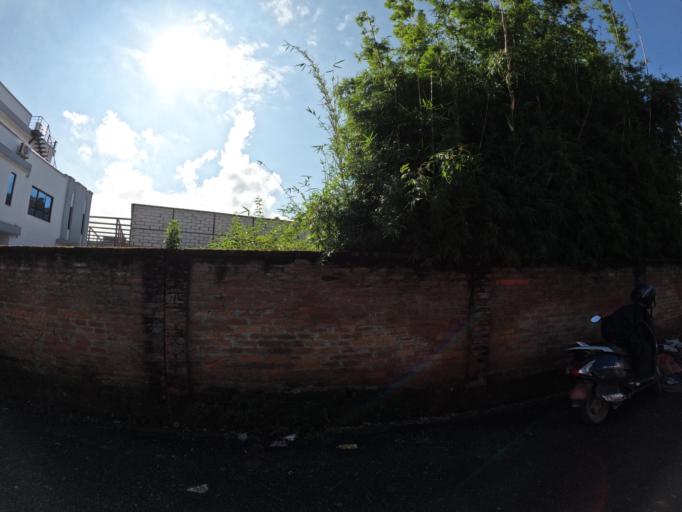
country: NP
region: Central Region
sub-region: Bagmati Zone
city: Kathmandu
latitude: 27.7553
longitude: 85.3284
